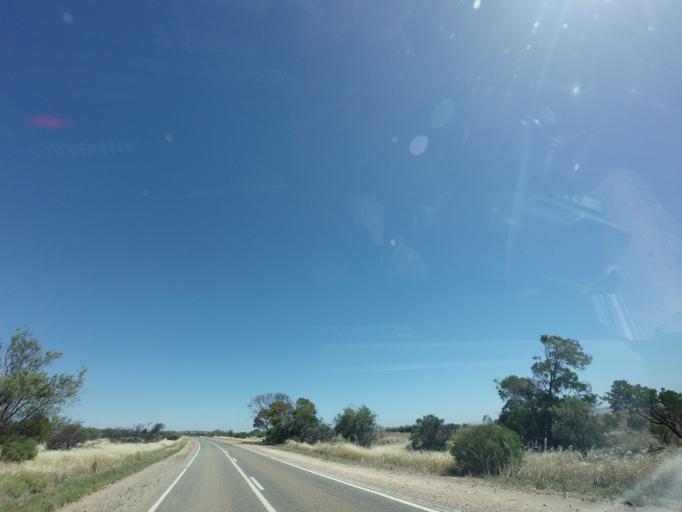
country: AU
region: South Australia
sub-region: Peterborough
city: Peterborough
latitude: -32.8792
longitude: 138.7399
